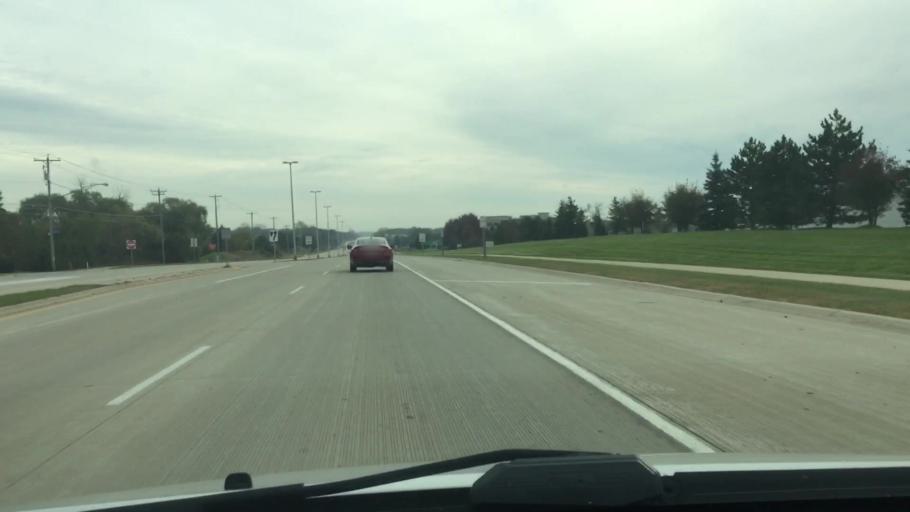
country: US
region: Wisconsin
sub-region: Milwaukee County
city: Franklin
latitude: 42.8723
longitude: -87.9753
